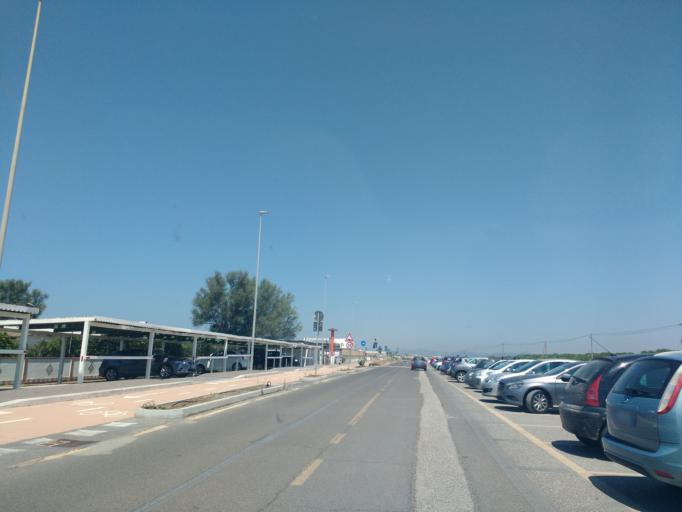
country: IT
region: Latium
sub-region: Citta metropolitana di Roma Capitale
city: Passo Oscuro
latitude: 41.8825
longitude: 12.1729
